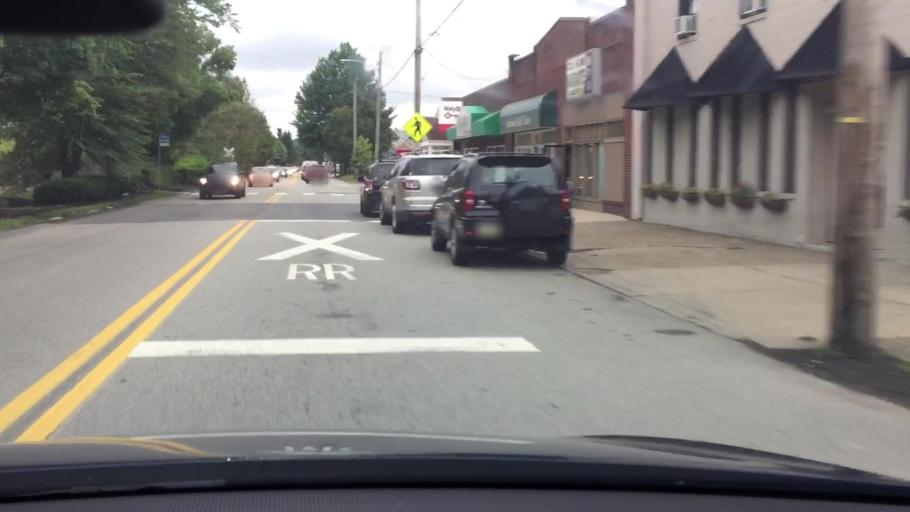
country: US
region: Pennsylvania
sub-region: Allegheny County
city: Oakmont
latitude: 40.5207
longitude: -79.8428
